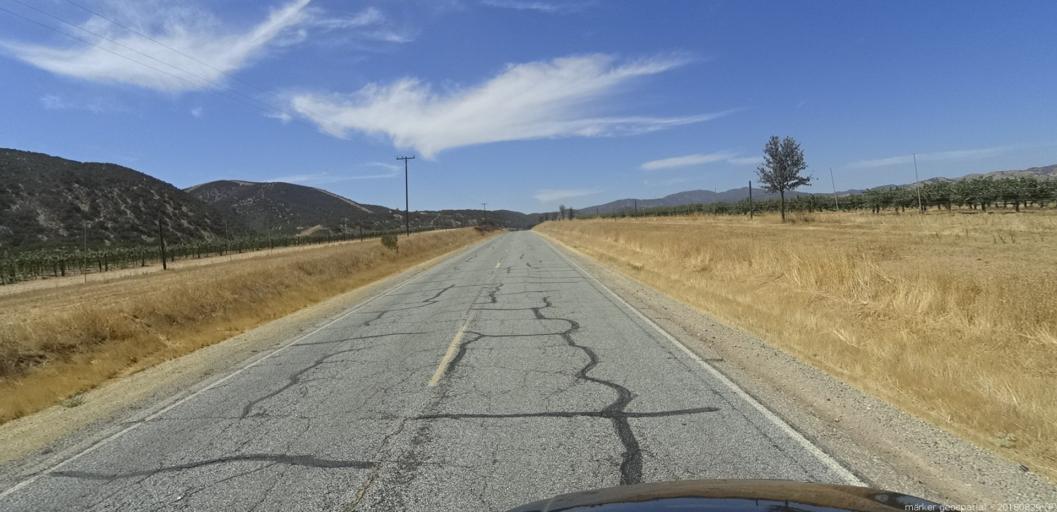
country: US
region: California
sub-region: San Luis Obispo County
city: Lake Nacimiento
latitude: 35.8840
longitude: -120.9115
